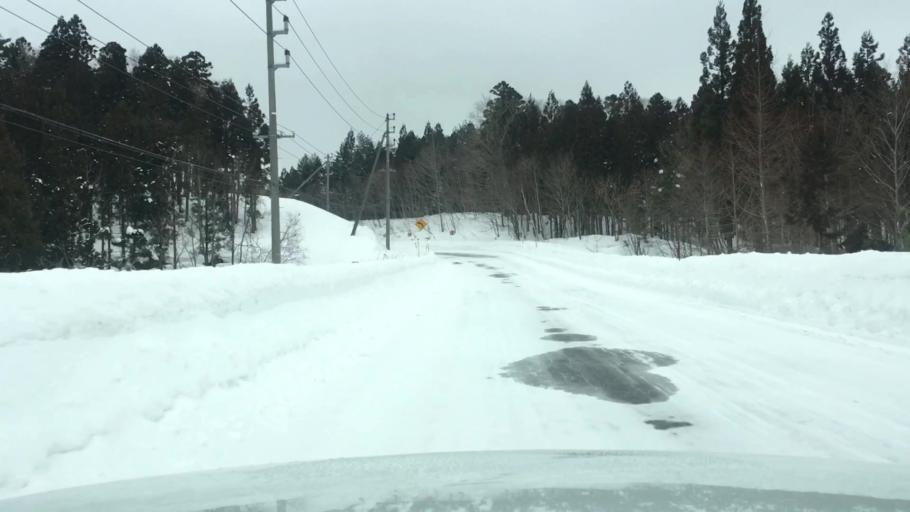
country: JP
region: Akita
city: Hanawa
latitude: 39.9984
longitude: 140.9897
